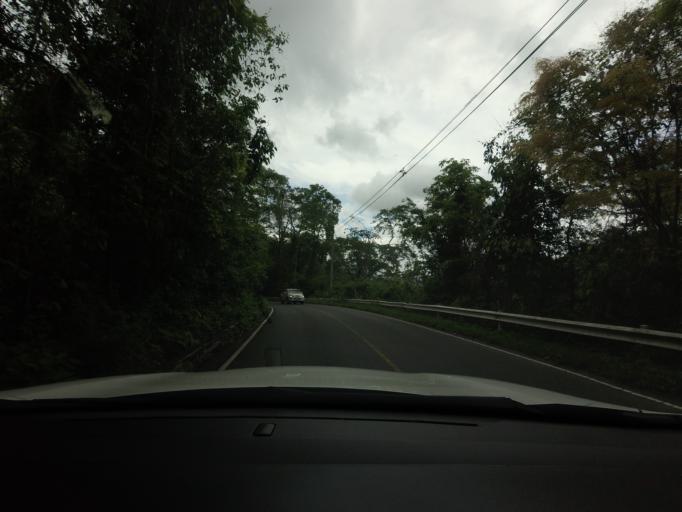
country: TH
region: Nakhon Ratchasima
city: Pak Chong
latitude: 14.4873
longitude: 101.3896
